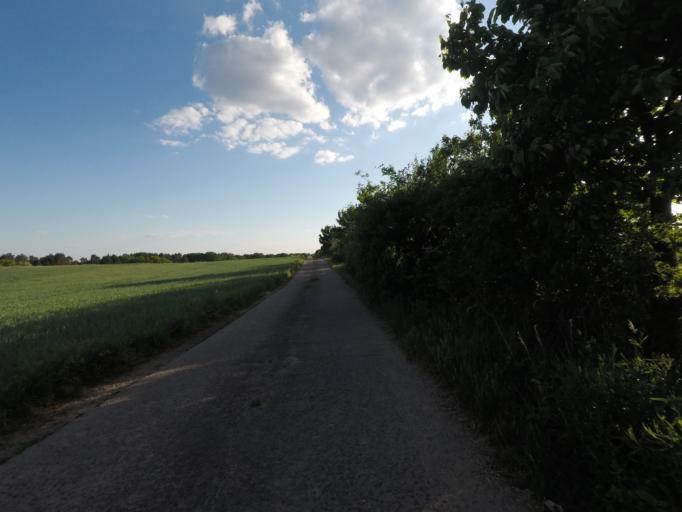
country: DE
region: Brandenburg
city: Melchow
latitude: 52.8672
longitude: 13.6947
